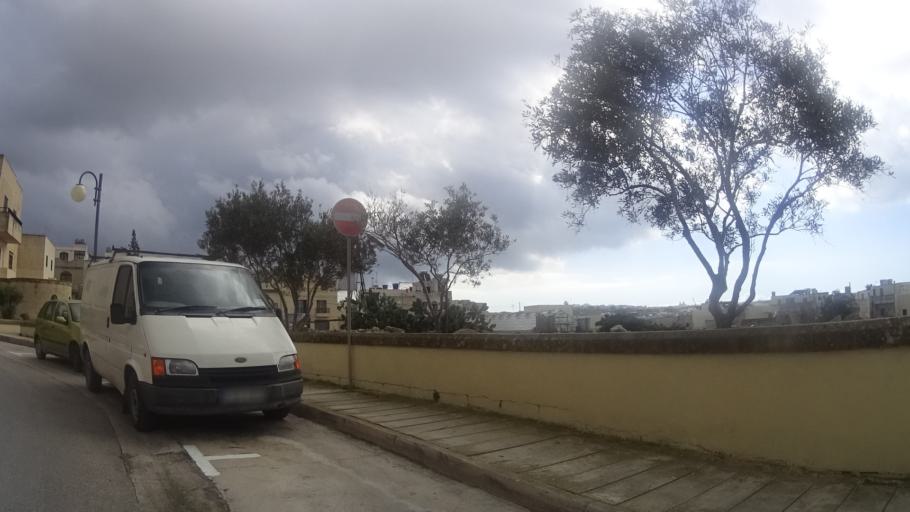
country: MT
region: L-Imtarfa
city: Imtarfa
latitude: 35.8887
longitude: 14.3929
